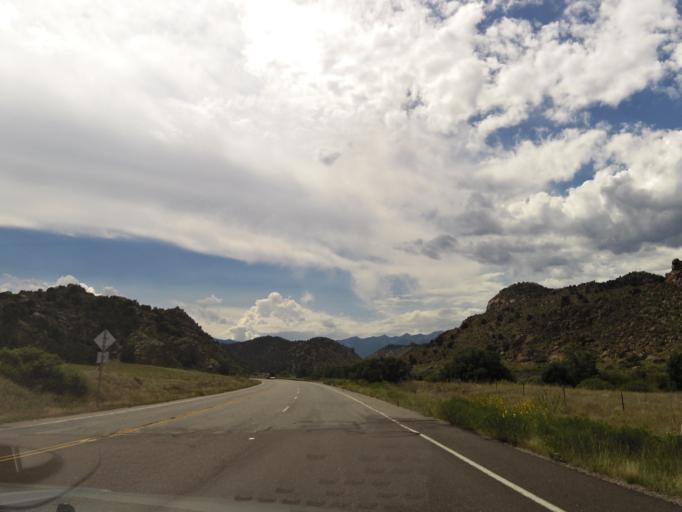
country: US
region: Colorado
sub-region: Custer County
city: Westcliffe
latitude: 38.3962
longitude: -105.6334
